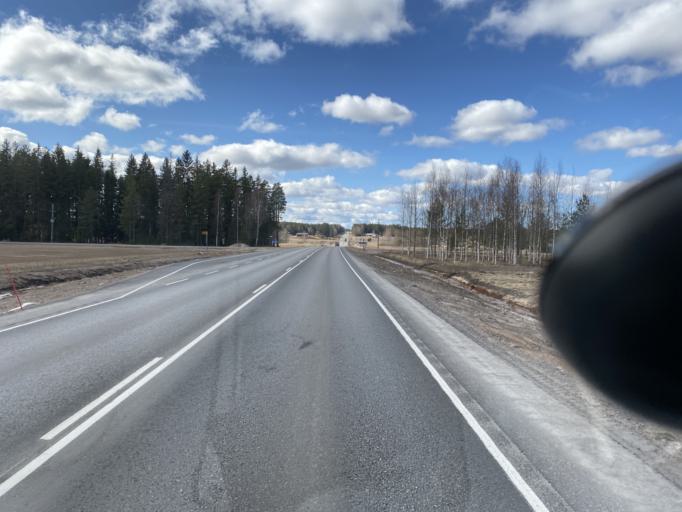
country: FI
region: Satakunta
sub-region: Rauma
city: Koeylioe
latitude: 61.1556
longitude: 22.2748
